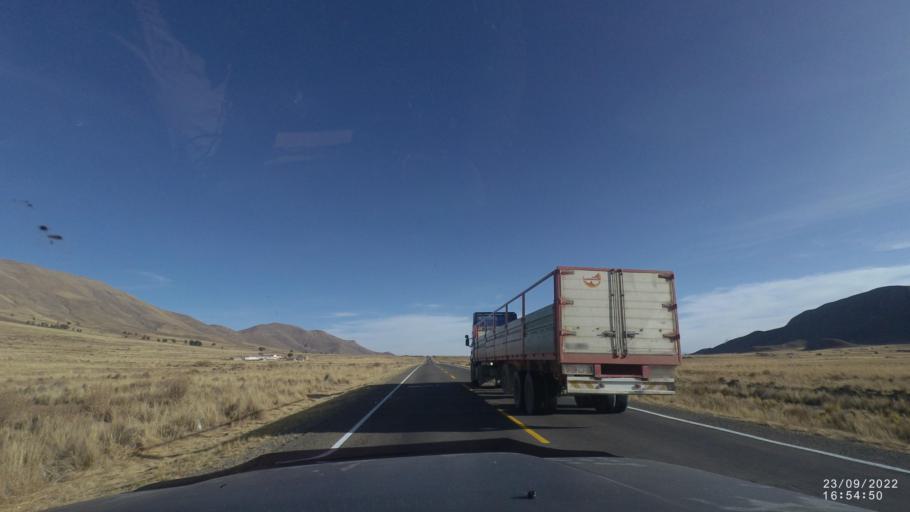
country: BO
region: Oruro
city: Poopo
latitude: -18.4703
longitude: -66.9679
